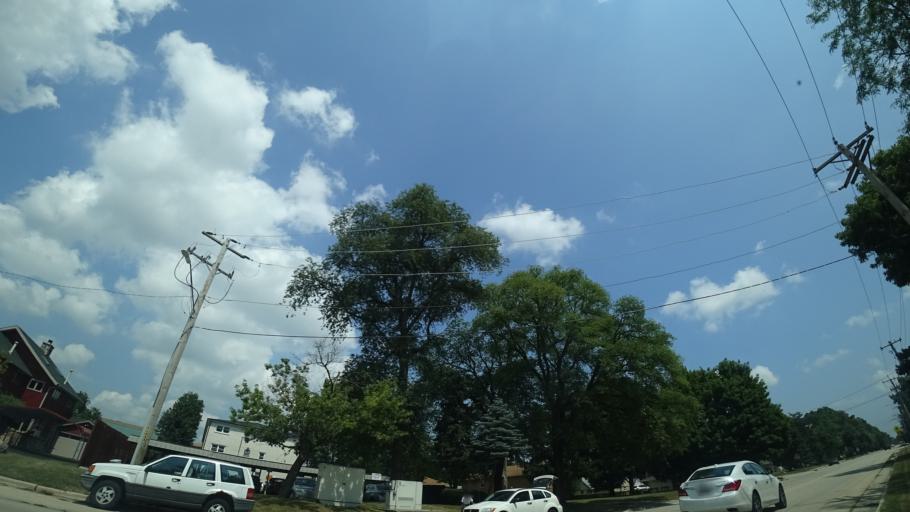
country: US
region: Illinois
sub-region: Cook County
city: Worth
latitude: 41.6972
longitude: -87.7954
